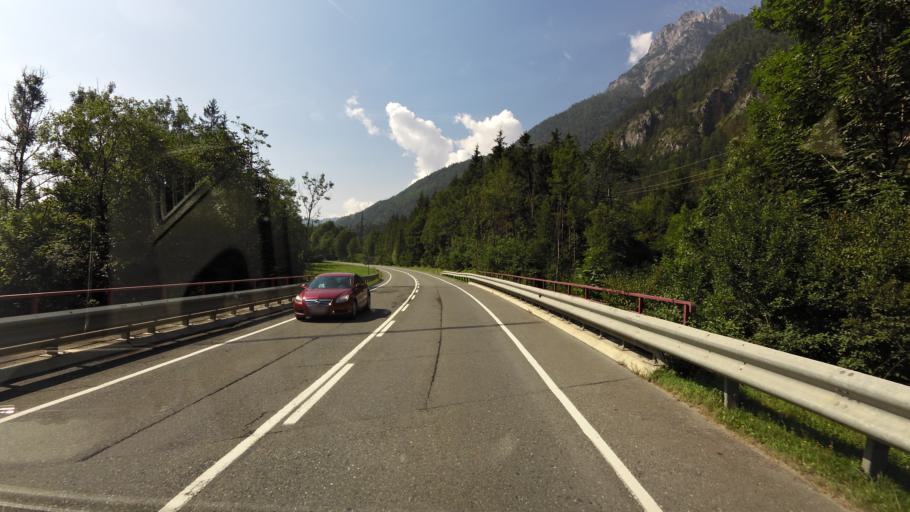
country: AT
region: Salzburg
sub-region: Politischer Bezirk Sankt Johann im Pongau
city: Werfen
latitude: 47.5184
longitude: 13.1645
